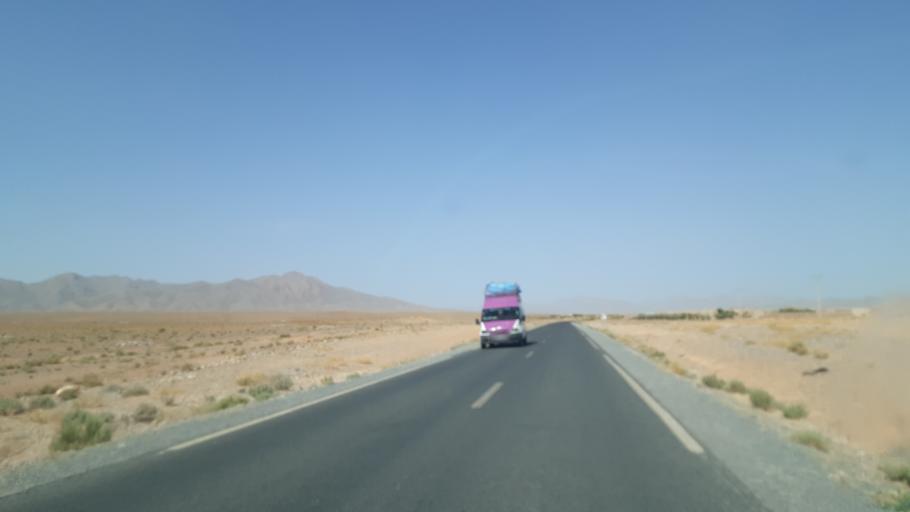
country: MA
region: Meknes-Tafilalet
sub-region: Errachidia
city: Amouguer
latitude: 32.2351
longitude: -4.6322
